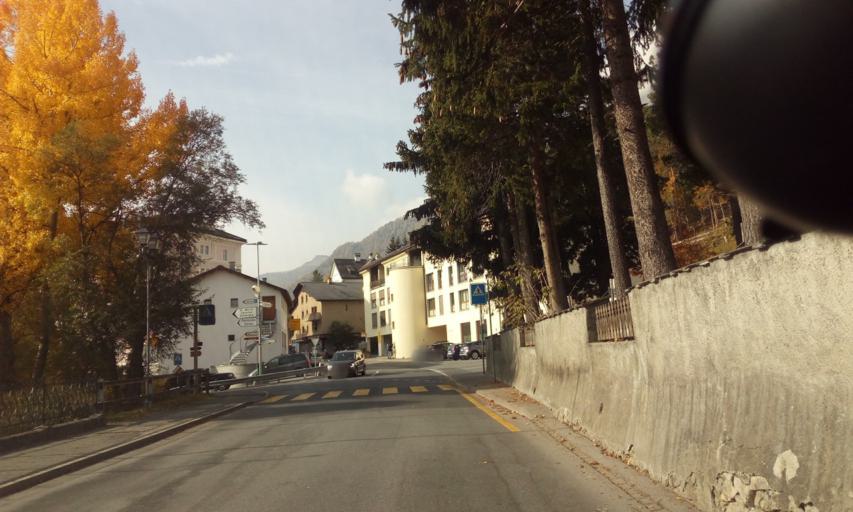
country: CH
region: Grisons
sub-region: Maloja District
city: Samedan
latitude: 46.5363
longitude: 9.8734
